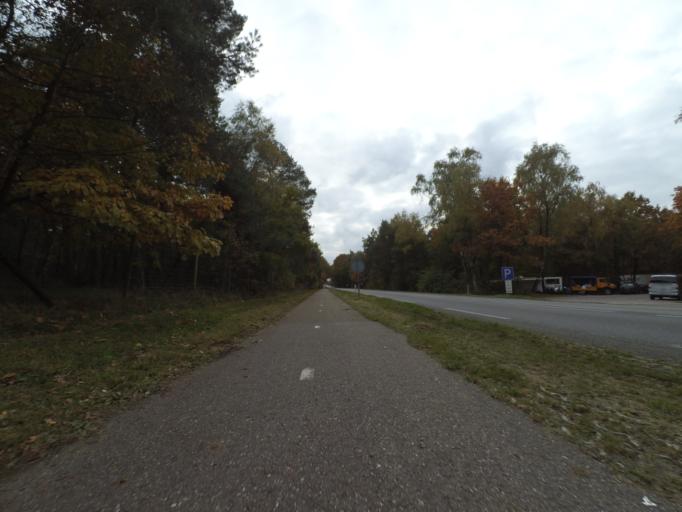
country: NL
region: Gelderland
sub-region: Gemeente Ermelo
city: Ermelo
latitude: 52.2986
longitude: 5.6798
